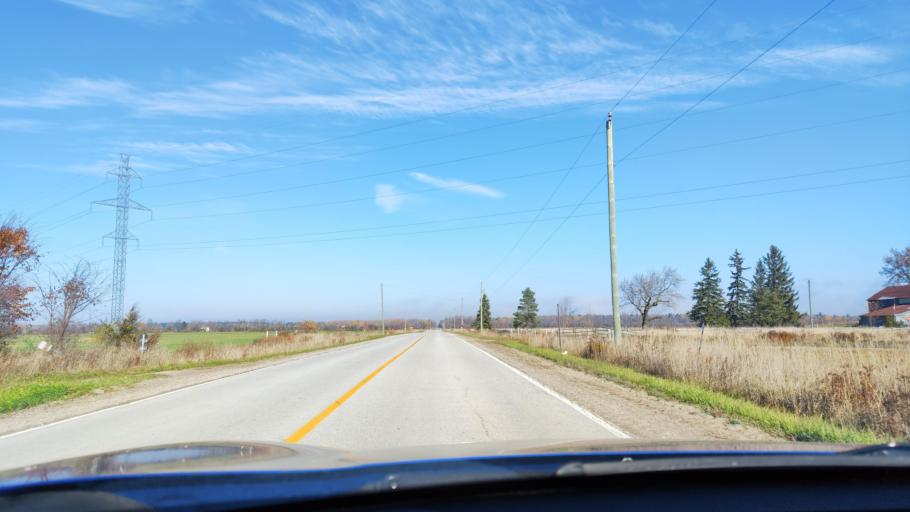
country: CA
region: Ontario
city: Wasaga Beach
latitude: 44.3924
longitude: -80.0561
